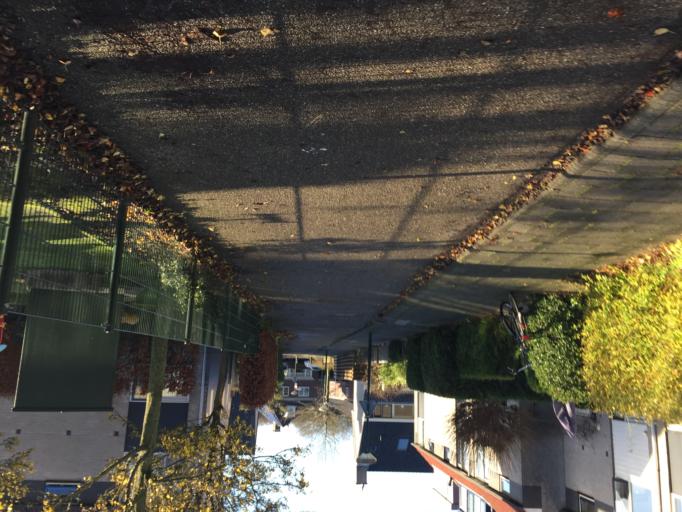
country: NL
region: Utrecht
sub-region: Stichtse Vecht
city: Breukelen
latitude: 52.1660
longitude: 5.0041
